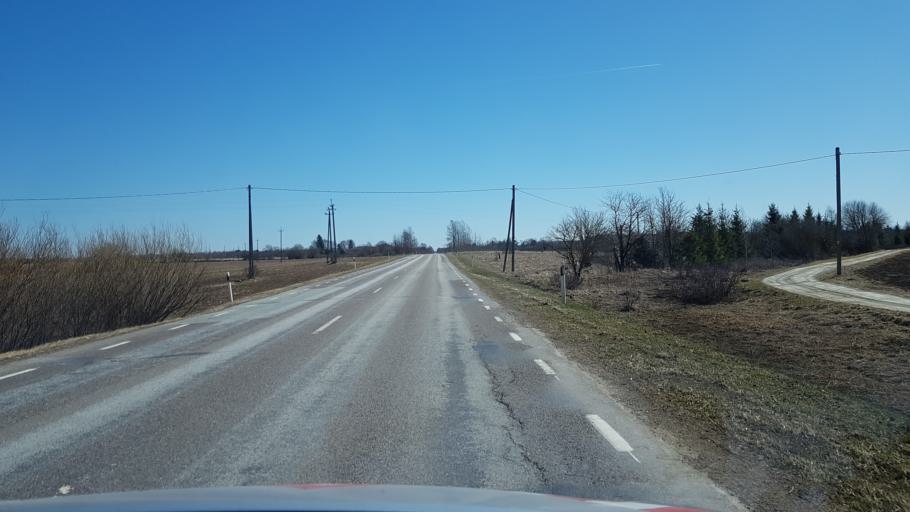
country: EE
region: Laeaene-Virumaa
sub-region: Viru-Nigula vald
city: Kunda
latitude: 59.4873
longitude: 26.5905
